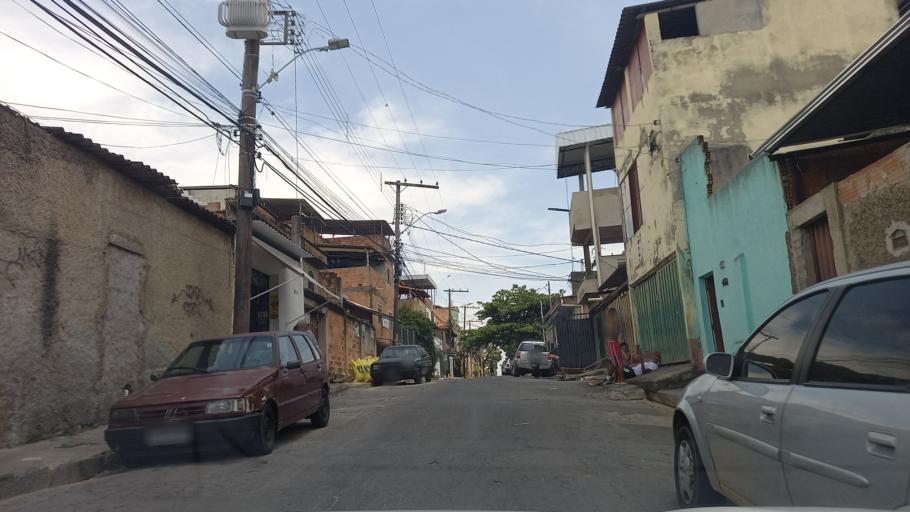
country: BR
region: Minas Gerais
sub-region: Contagem
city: Contagem
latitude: -19.9092
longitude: -44.0092
